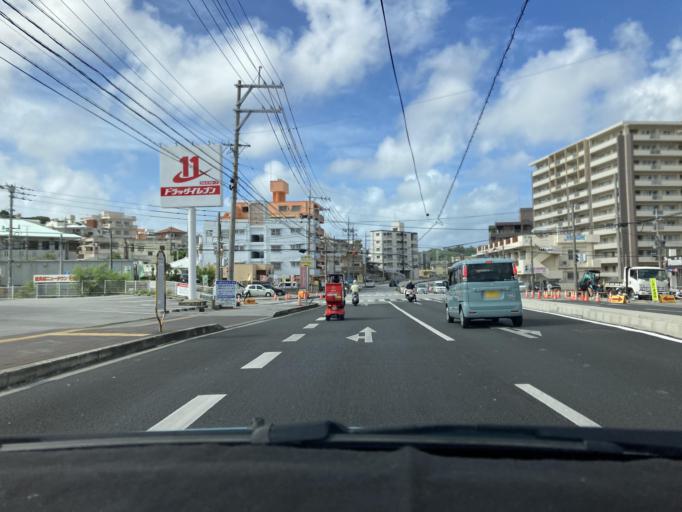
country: JP
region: Okinawa
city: Tomigusuku
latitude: 26.1912
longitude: 127.6927
